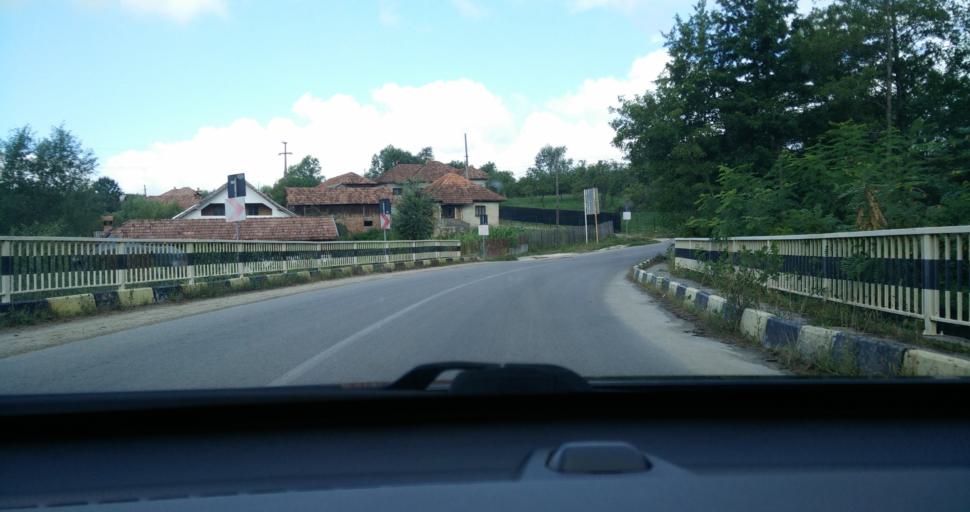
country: RO
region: Gorj
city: Novaci-Straini
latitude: 45.1760
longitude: 23.7068
